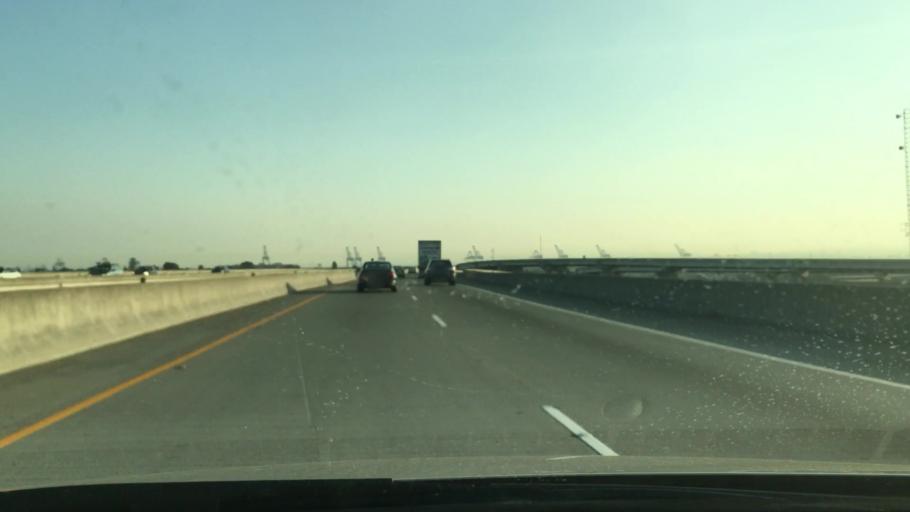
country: US
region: California
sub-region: Alameda County
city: Emeryville
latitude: 37.8222
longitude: -122.2926
